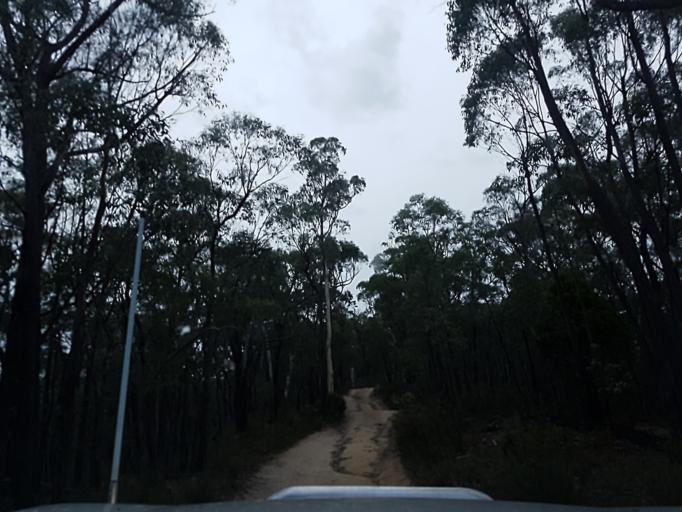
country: AU
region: New South Wales
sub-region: Snowy River
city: Jindabyne
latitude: -36.8581
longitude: 148.2327
